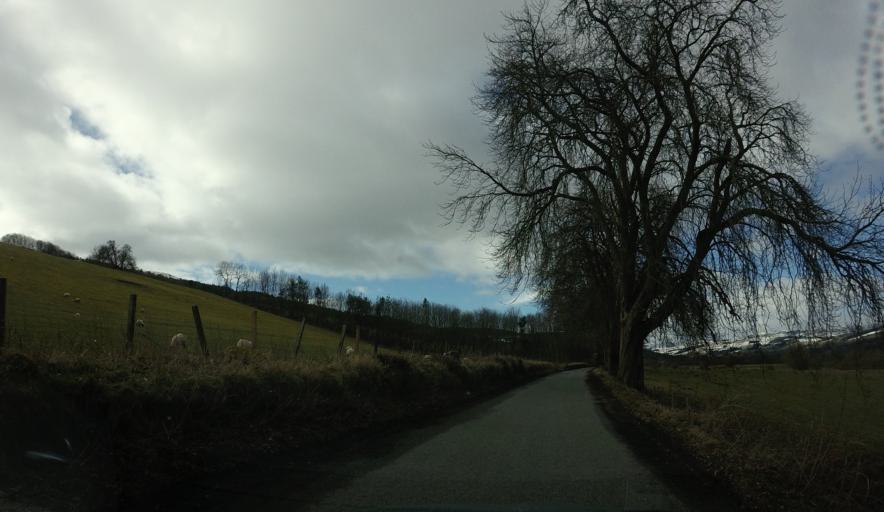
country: GB
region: Scotland
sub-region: Perth and Kinross
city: Pitlochry
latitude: 56.6445
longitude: -3.6959
